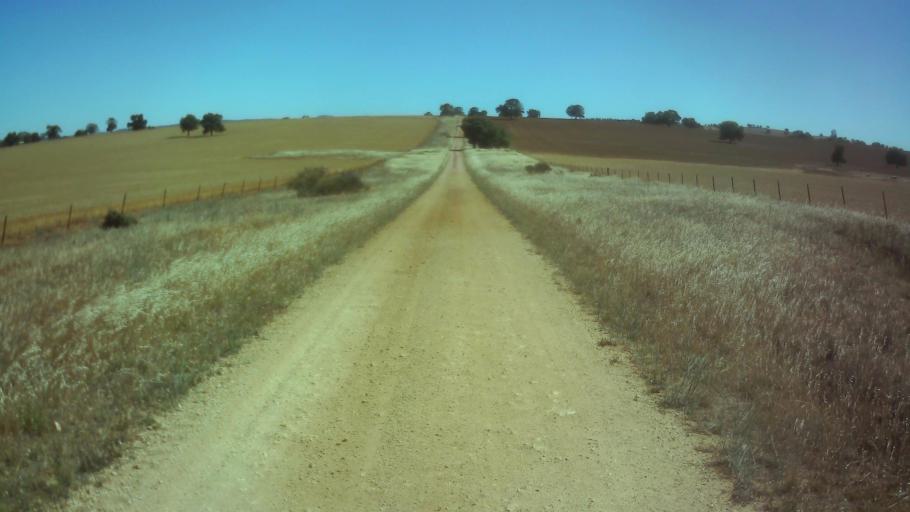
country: AU
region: New South Wales
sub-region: Weddin
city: Grenfell
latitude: -33.9745
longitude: 148.3430
